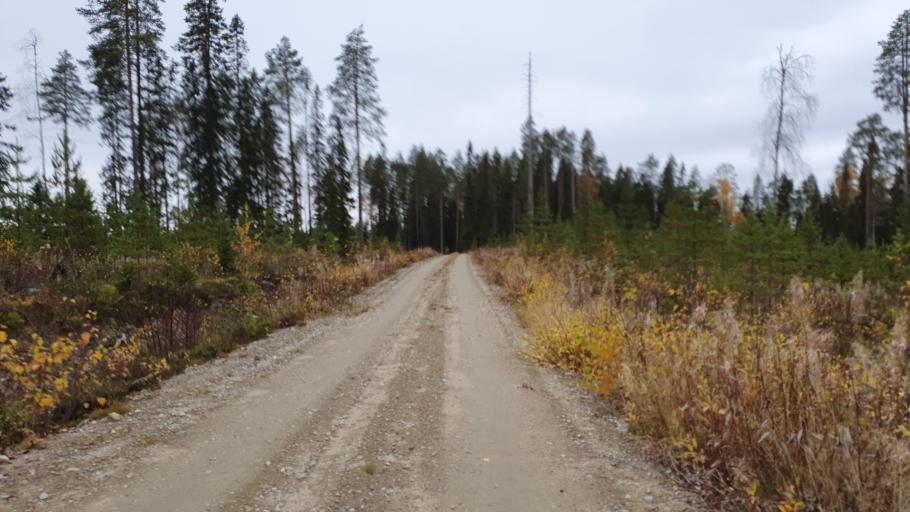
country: FI
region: Kainuu
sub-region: Kehys-Kainuu
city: Kuhmo
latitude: 64.4525
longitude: 29.6202
